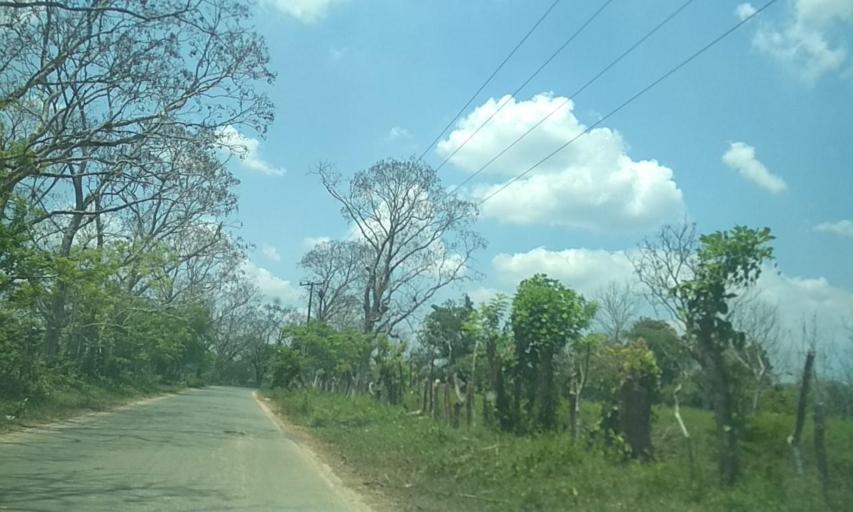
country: MX
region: Tabasco
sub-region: Huimanguillo
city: Francisco Rueda
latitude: 17.8249
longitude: -93.9348
